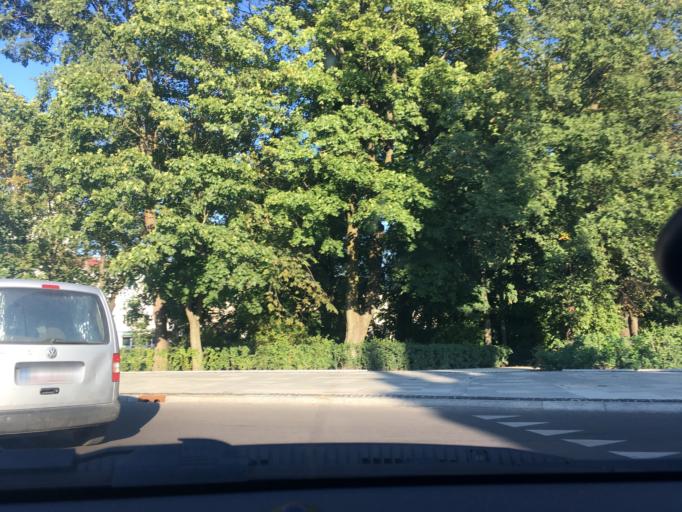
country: PL
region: Podlasie
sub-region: Bialystok
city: Bialystok
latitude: 53.1317
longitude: 23.1677
